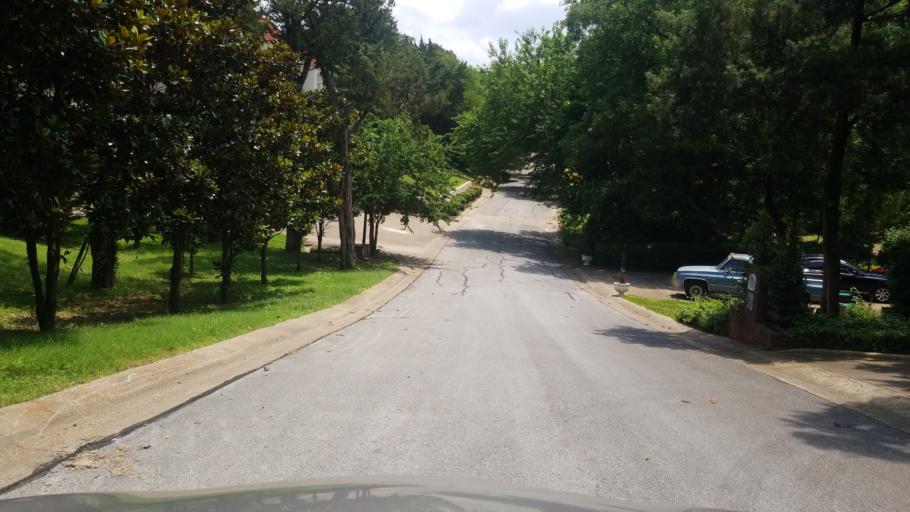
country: US
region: Texas
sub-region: Dallas County
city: Duncanville
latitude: 32.6760
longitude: -96.9172
